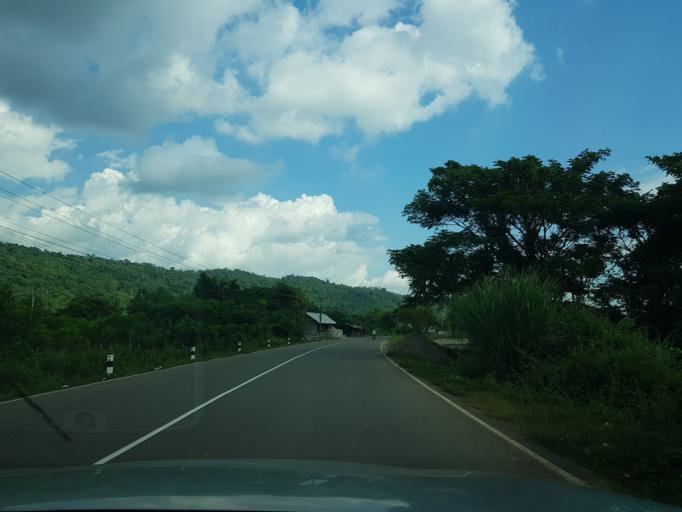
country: TH
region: Nong Khai
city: Sangkhom
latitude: 18.0239
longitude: 102.3871
